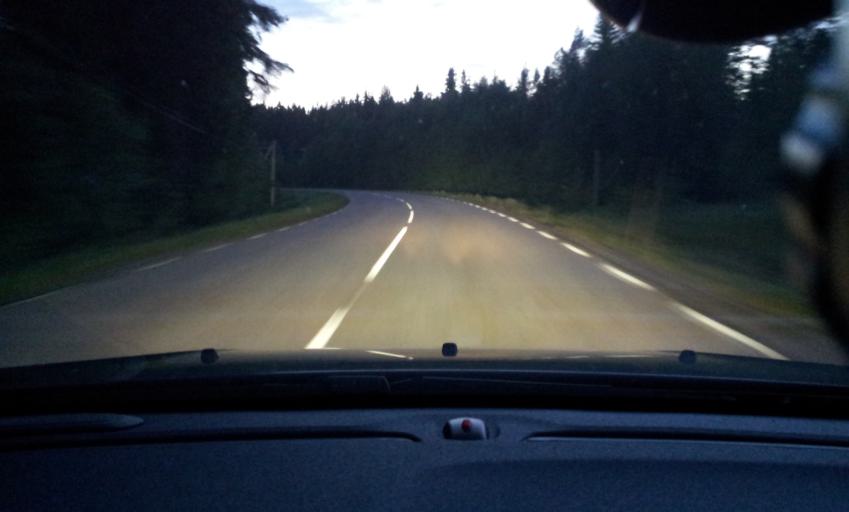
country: SE
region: Jaemtland
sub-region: OEstersunds Kommun
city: Brunflo
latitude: 62.6626
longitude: 14.8567
